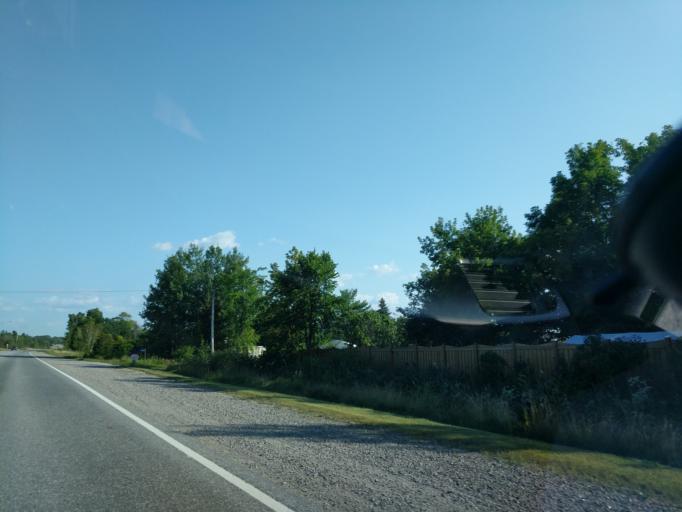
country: CA
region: Quebec
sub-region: Outaouais
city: Wakefield
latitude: 45.5178
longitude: -75.9850
